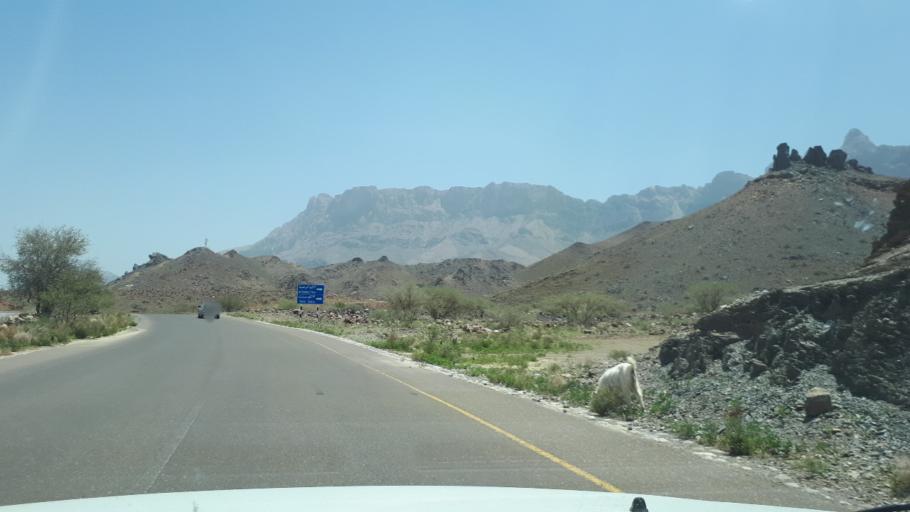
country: OM
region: Muhafazat ad Dakhiliyah
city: Bahla'
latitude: 23.1751
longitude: 57.1465
